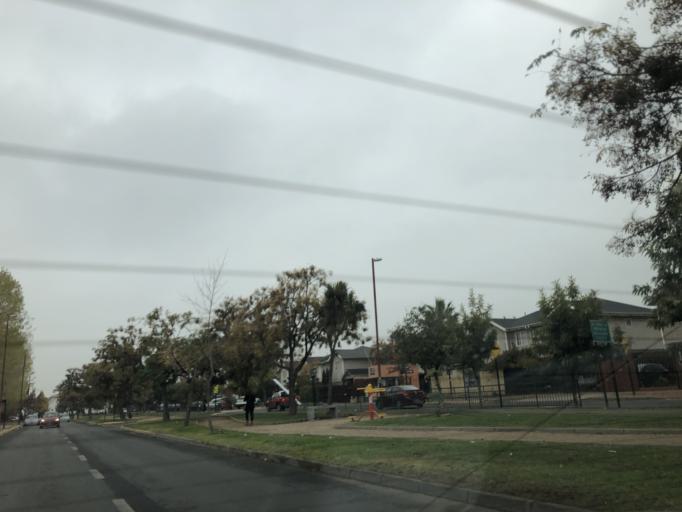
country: CL
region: Santiago Metropolitan
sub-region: Provincia de Cordillera
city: Puente Alto
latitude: -33.5956
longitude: -70.5826
